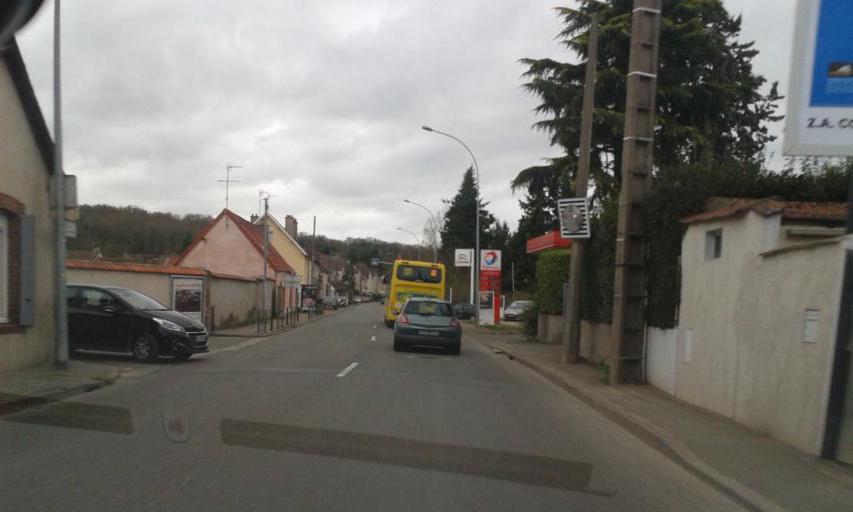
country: FR
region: Centre
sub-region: Departement d'Eure-et-Loir
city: Leves
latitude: 48.4636
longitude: 1.4814
